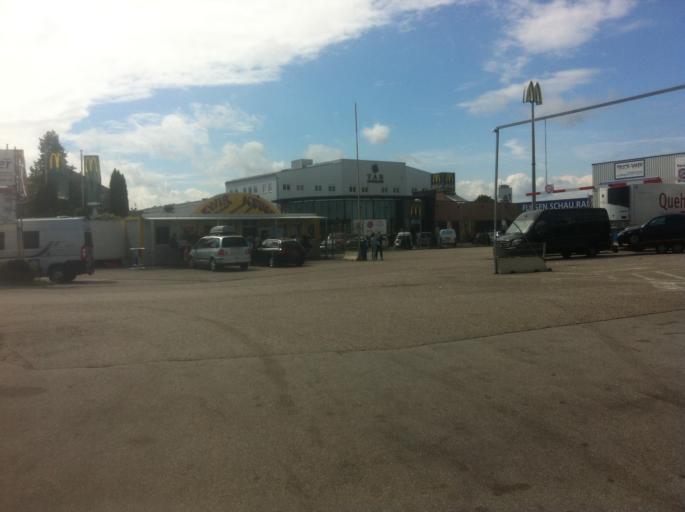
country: AT
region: Upper Austria
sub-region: Politischer Bezirk Linz-Land
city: Ansfelden
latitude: 48.2112
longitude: 14.2807
